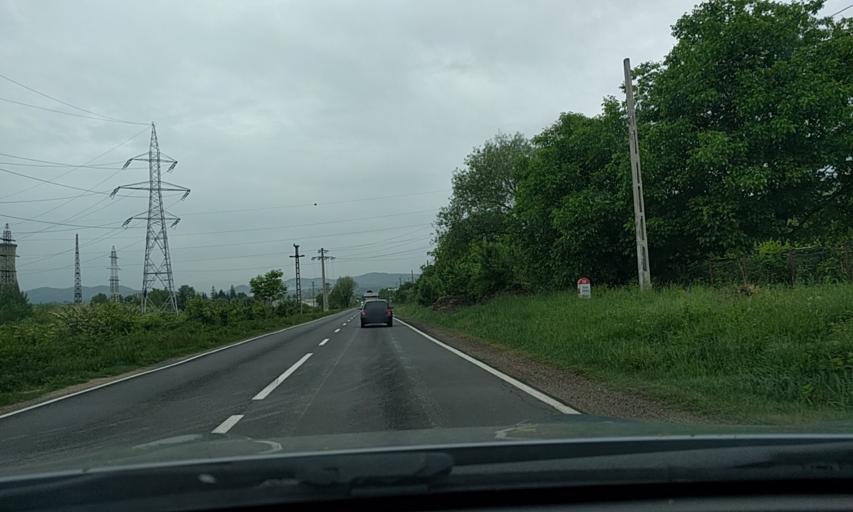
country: RO
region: Dambovita
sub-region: Comuna Doicesti
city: Doicesti
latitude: 45.0004
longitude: 25.4016
